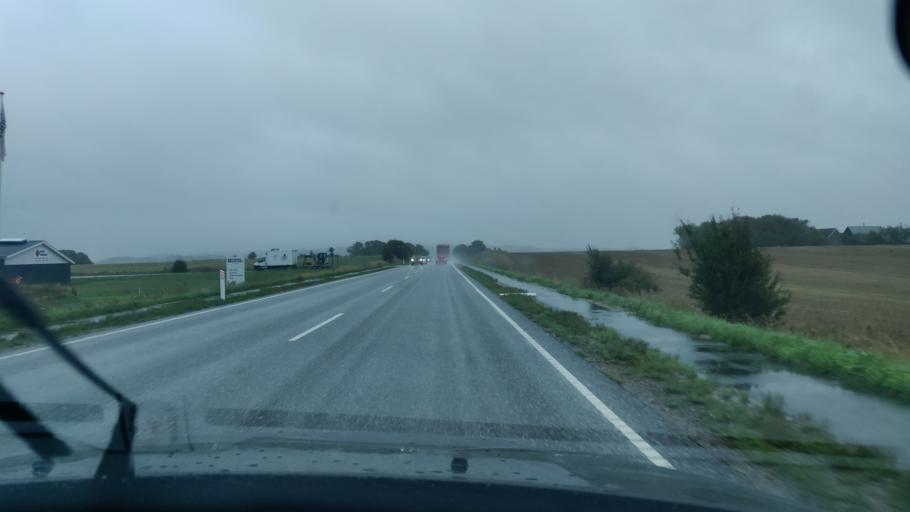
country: DK
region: North Denmark
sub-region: Thisted Kommune
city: Thisted
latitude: 56.8823
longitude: 8.6092
